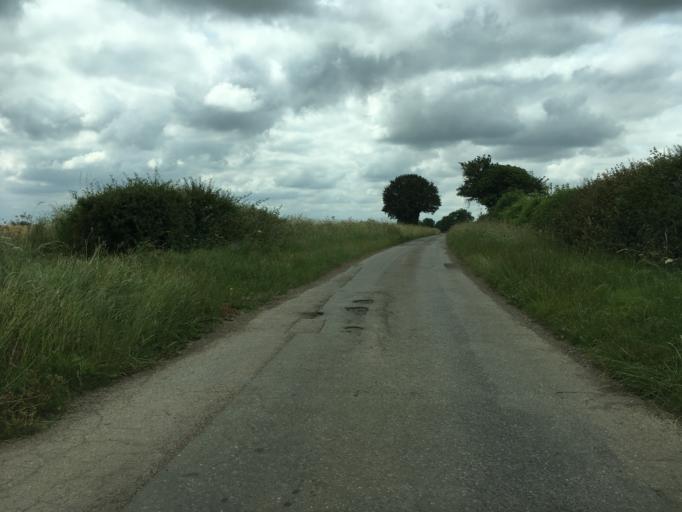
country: GB
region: England
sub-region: Oxfordshire
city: Chipping Norton
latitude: 51.9192
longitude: -1.5042
